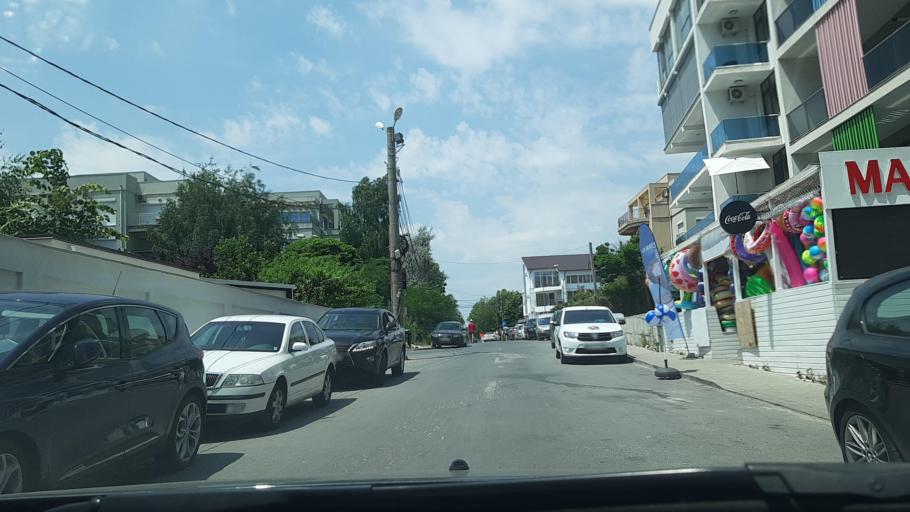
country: RO
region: Constanta
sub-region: Comuna Navodari
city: Navodari
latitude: 44.2998
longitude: 28.6247
